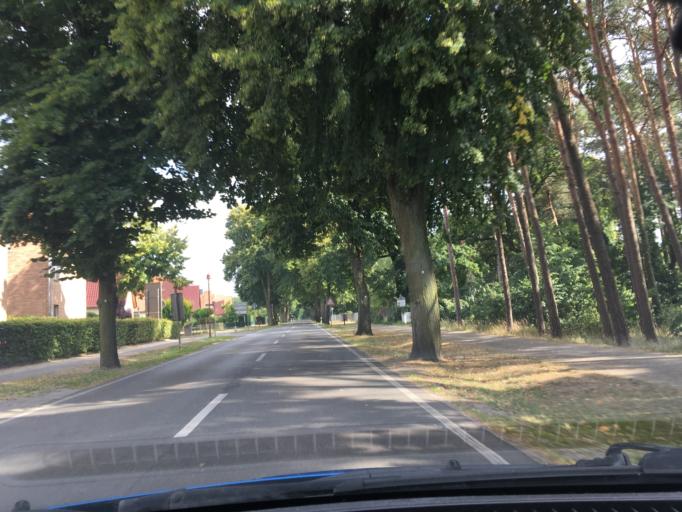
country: DE
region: Mecklenburg-Vorpommern
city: Lubtheen
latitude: 53.2965
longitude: 11.0857
